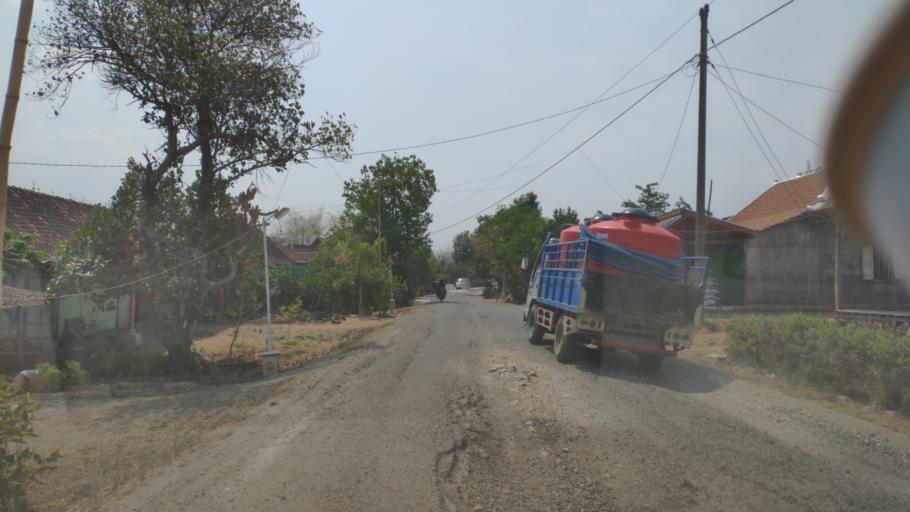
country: ID
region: Central Java
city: Kadengan
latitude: -7.1836
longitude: 111.3687
